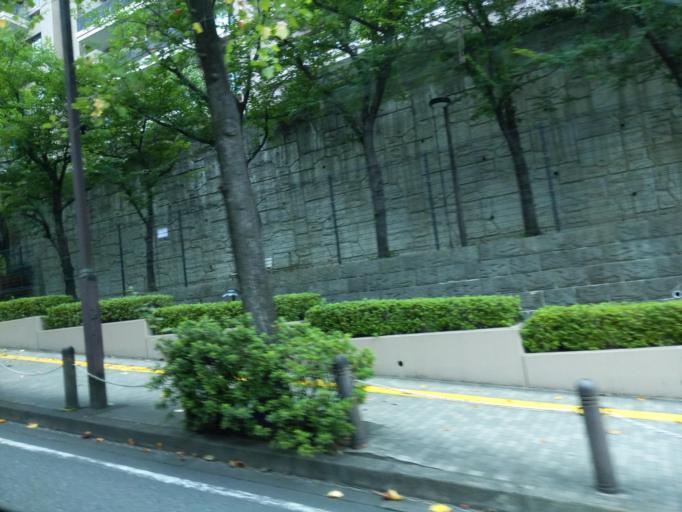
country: JP
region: Tokyo
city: Chofugaoka
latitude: 35.5862
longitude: 139.5808
